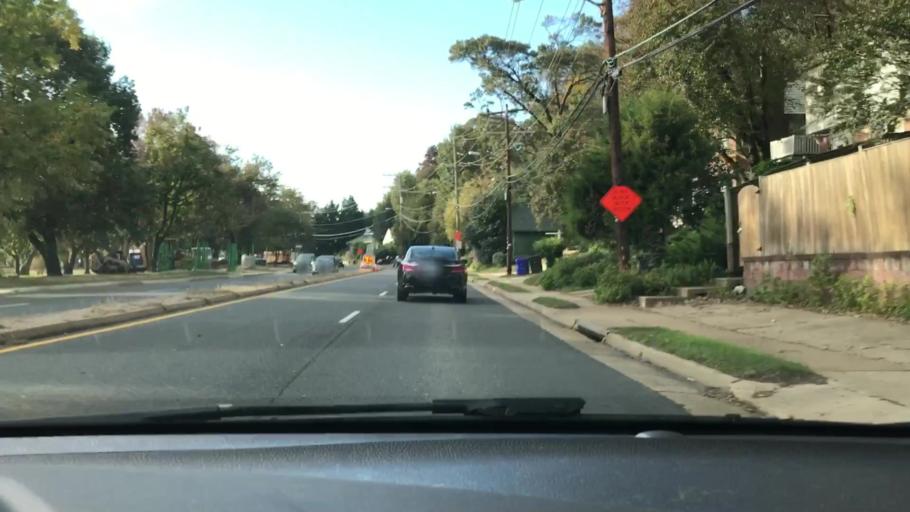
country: US
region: Virginia
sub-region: City of Alexandria
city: Alexandria
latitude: 38.8449
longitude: -77.0617
